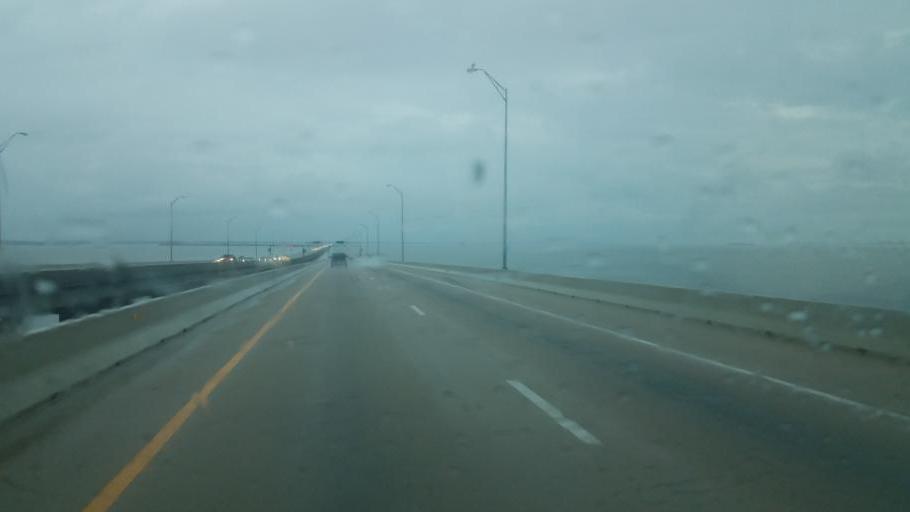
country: US
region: Virginia
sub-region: City of Newport News
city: Newport News
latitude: 36.9207
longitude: -76.4125
